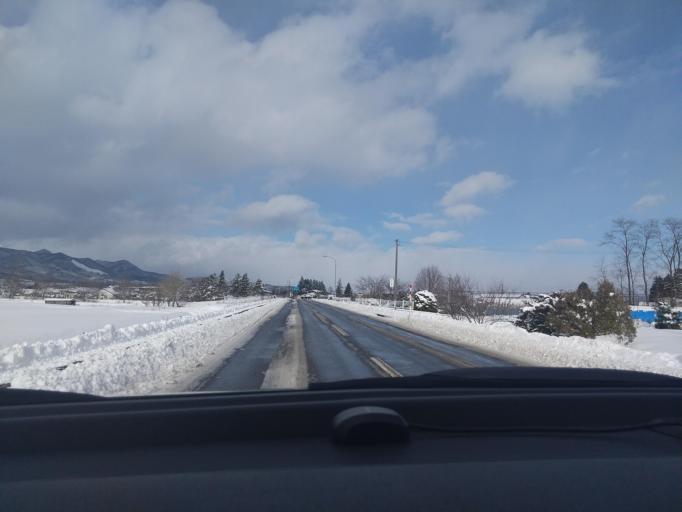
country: JP
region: Iwate
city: Morioka-shi
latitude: 39.5542
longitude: 141.1038
